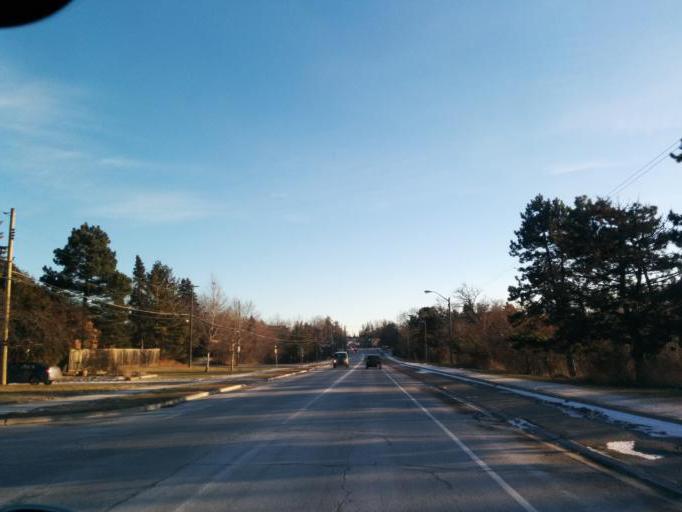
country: CA
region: Ontario
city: Etobicoke
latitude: 43.6602
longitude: -79.5566
